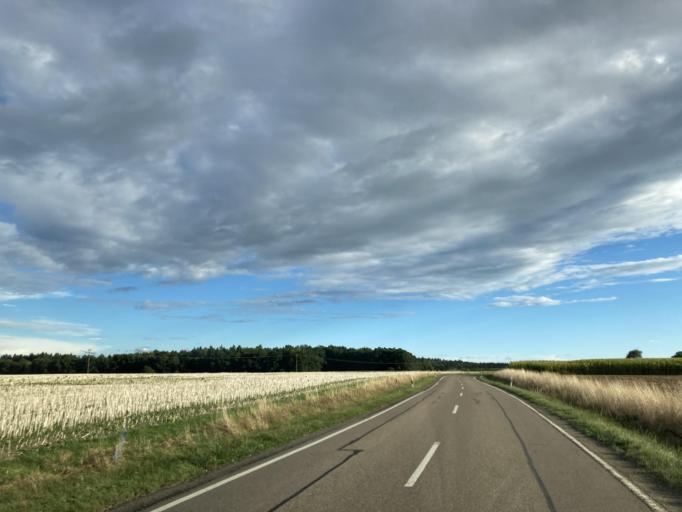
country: DE
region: Bavaria
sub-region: Swabia
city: Amerdingen
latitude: 48.7107
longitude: 10.4391
